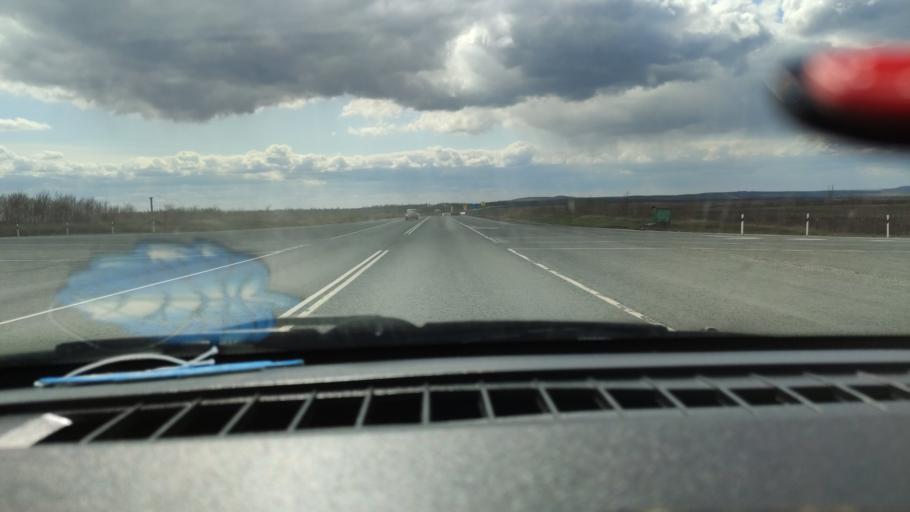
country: RU
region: Saratov
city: Alekseyevka
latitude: 52.2883
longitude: 47.9304
